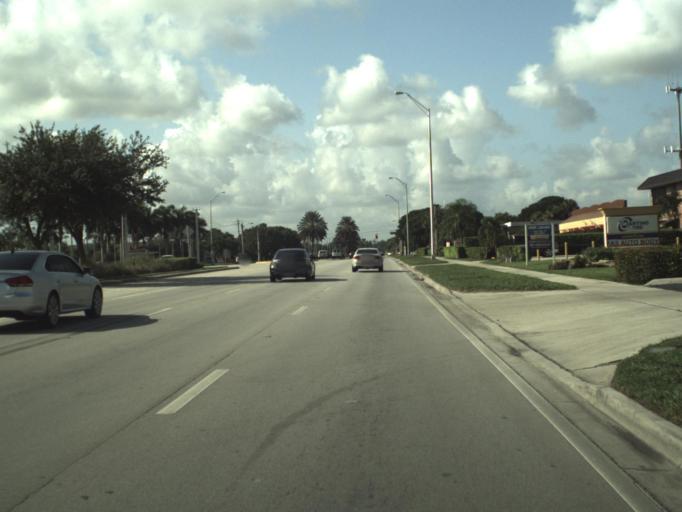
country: US
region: Florida
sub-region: Broward County
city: Margate
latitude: 26.2569
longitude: -80.2017
